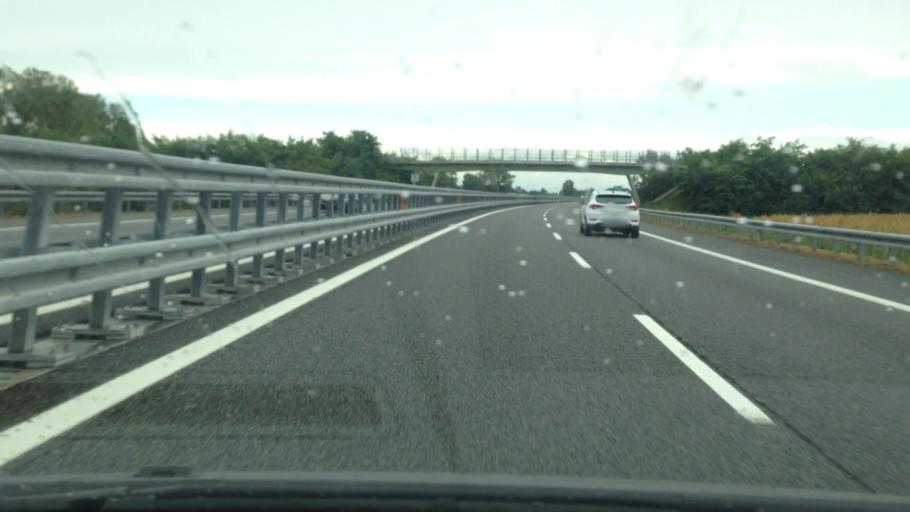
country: IT
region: Piedmont
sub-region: Provincia di Alessandria
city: Valle San Bartolomeo
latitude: 44.9412
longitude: 8.6498
